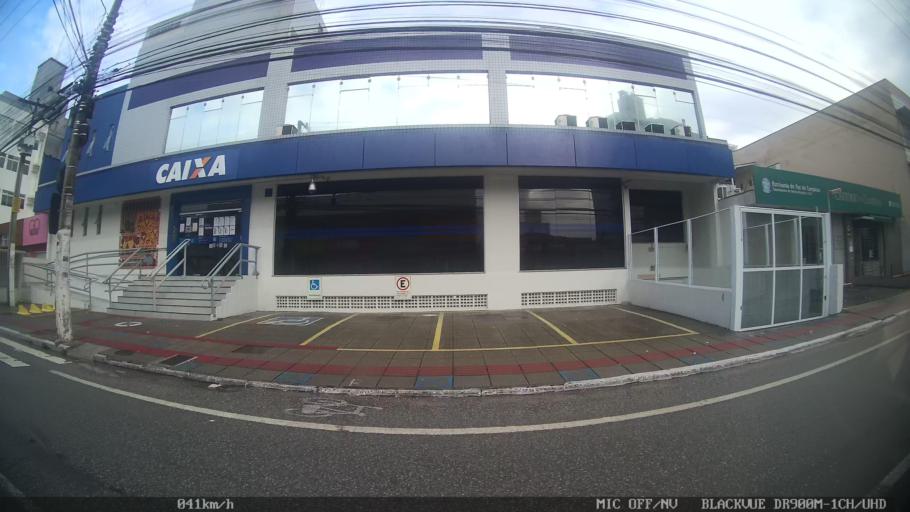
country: BR
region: Santa Catarina
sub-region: Sao Jose
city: Campinas
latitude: -27.5914
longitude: -48.6122
